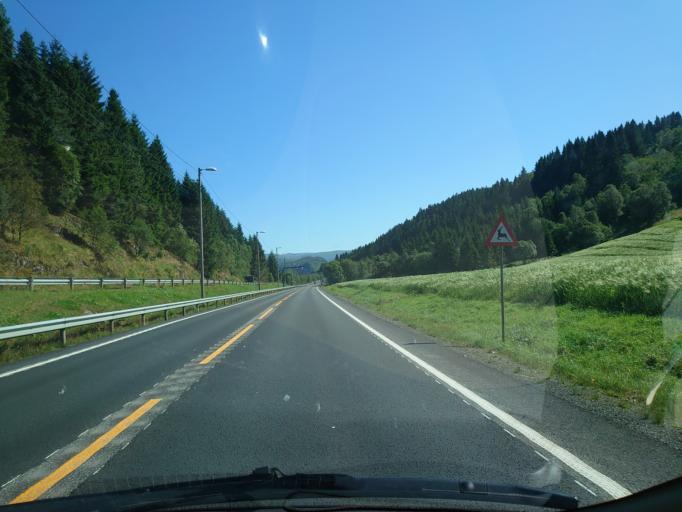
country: NO
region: Hordaland
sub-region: Bergen
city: Hylkje
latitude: 60.4711
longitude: 5.3667
